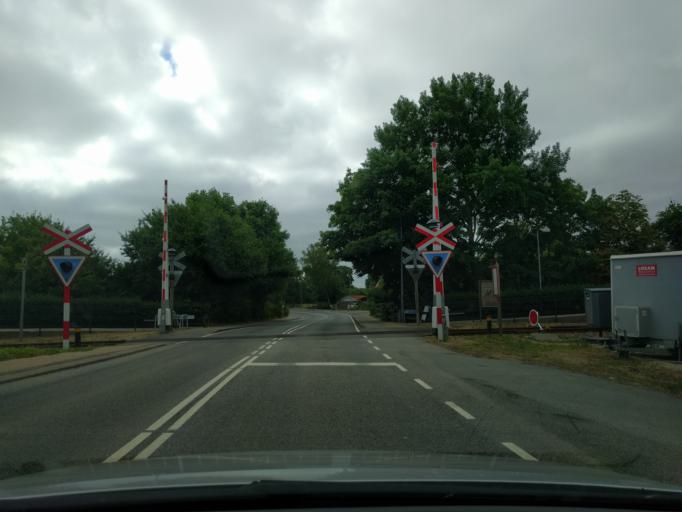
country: DK
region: Capital Region
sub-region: Helsingor Kommune
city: Espergaerde
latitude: 56.0023
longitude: 12.5325
